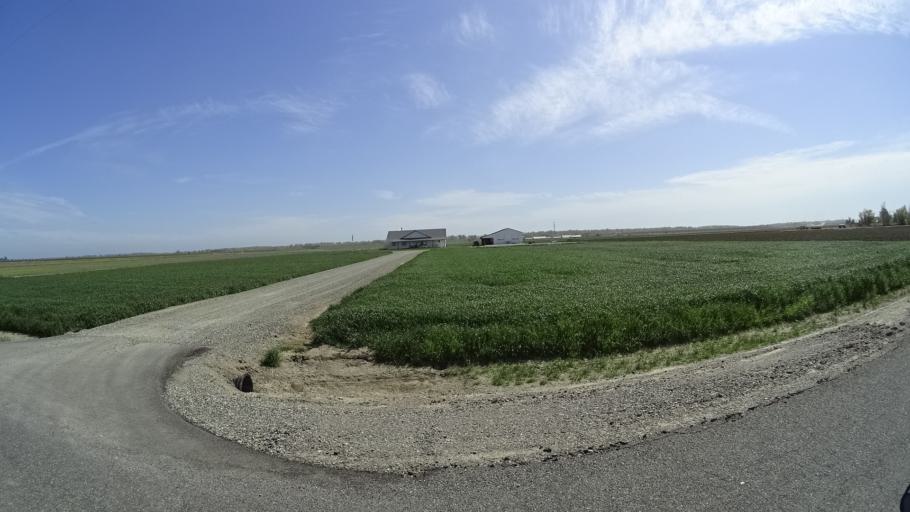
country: US
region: California
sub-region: Glenn County
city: Hamilton City
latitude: 39.5866
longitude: -122.0275
